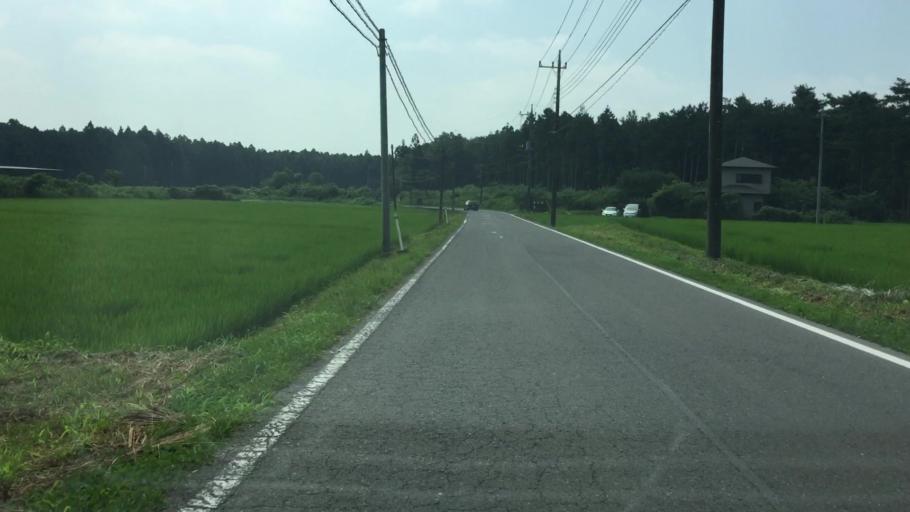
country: JP
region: Tochigi
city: Kuroiso
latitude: 36.9573
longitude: 139.9563
